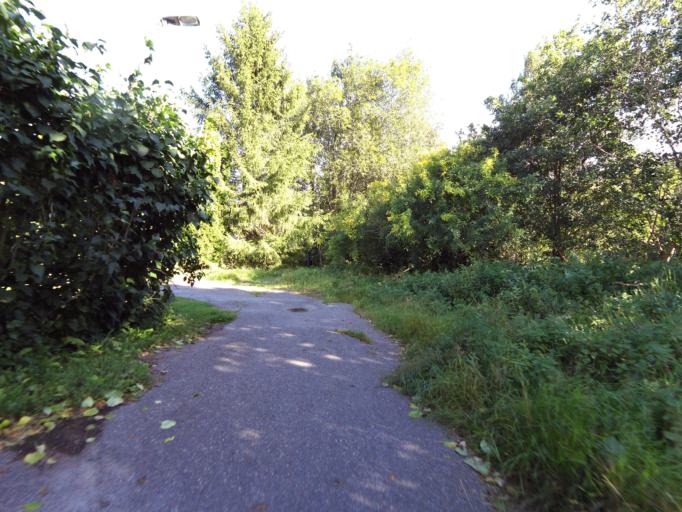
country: SE
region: Gaevleborg
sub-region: Gavle Kommun
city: Gavle
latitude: 60.6666
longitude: 17.2175
